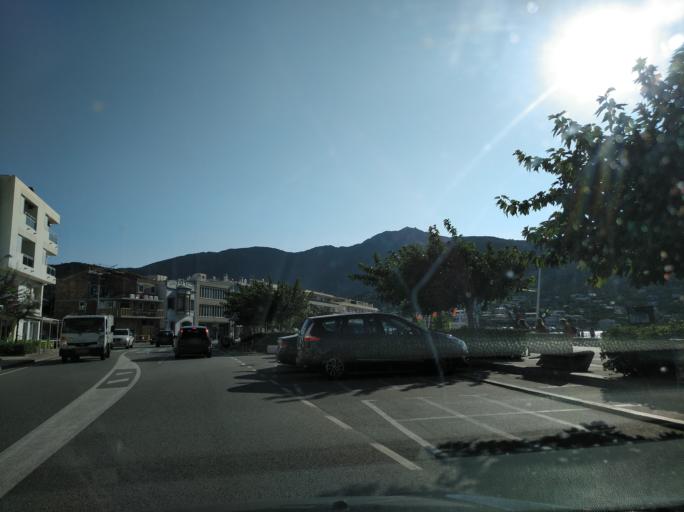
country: ES
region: Catalonia
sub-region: Provincia de Girona
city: Llanca
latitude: 42.3361
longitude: 3.2031
